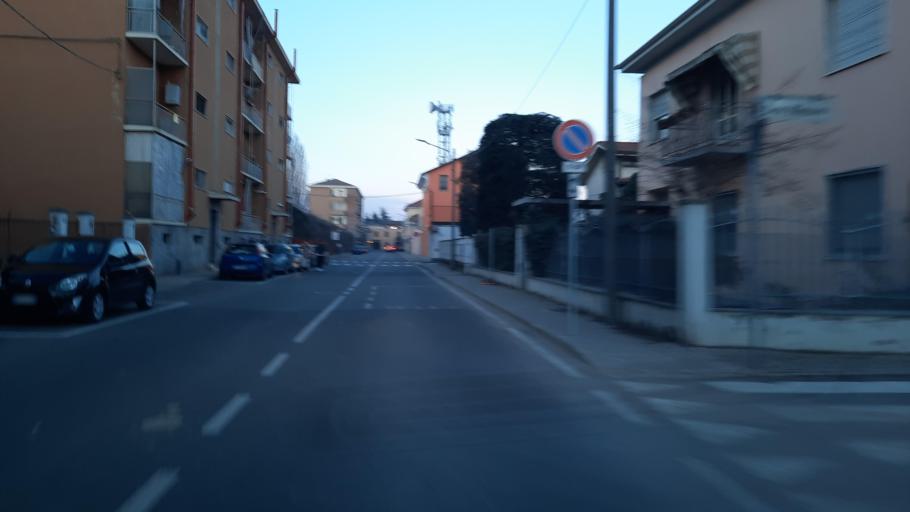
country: IT
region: Piedmont
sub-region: Provincia di Vercelli
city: Trino
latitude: 45.1921
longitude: 8.2994
